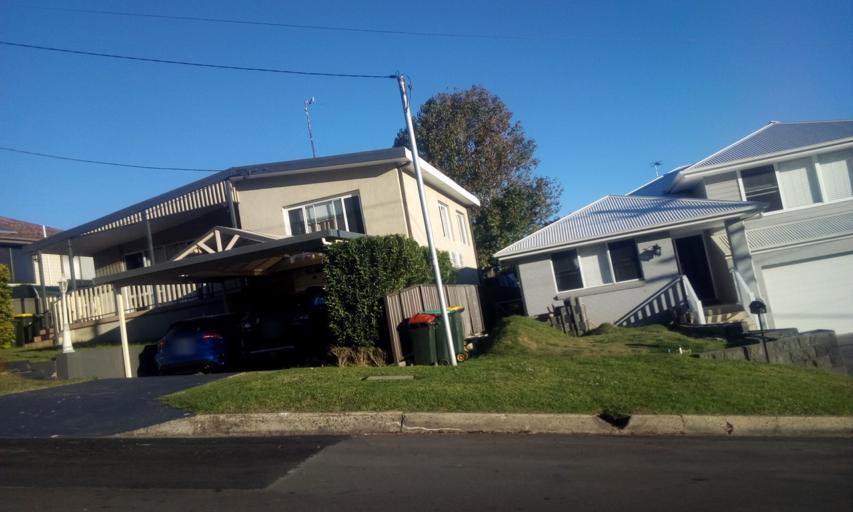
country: AU
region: New South Wales
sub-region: Wollongong
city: West Wollongong
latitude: -34.4321
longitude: 150.8541
